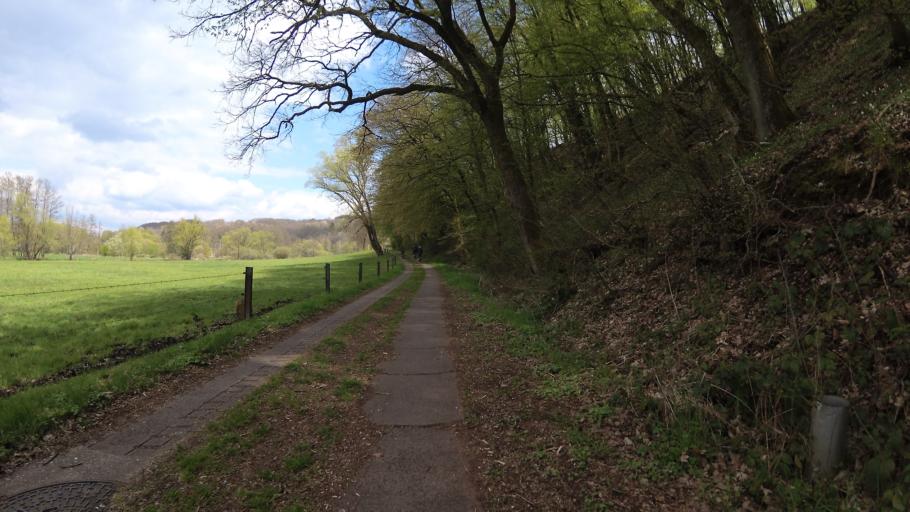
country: DE
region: Saarland
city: Schmelz
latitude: 49.4884
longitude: 6.8477
